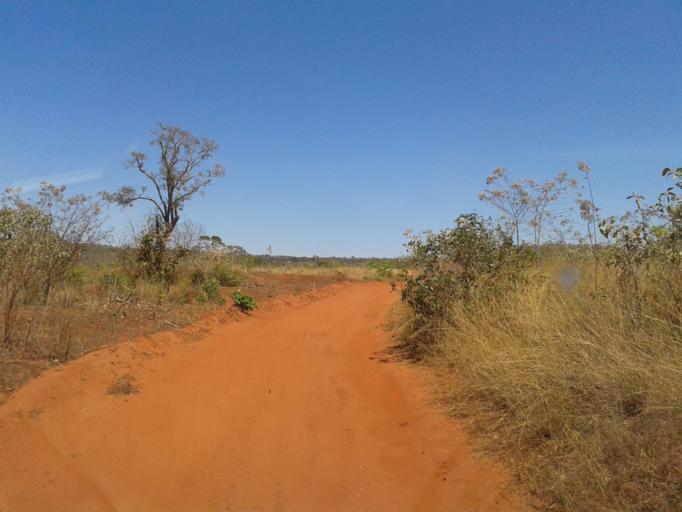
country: BR
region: Minas Gerais
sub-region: Ituiutaba
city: Ituiutaba
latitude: -19.1119
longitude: -49.2848
